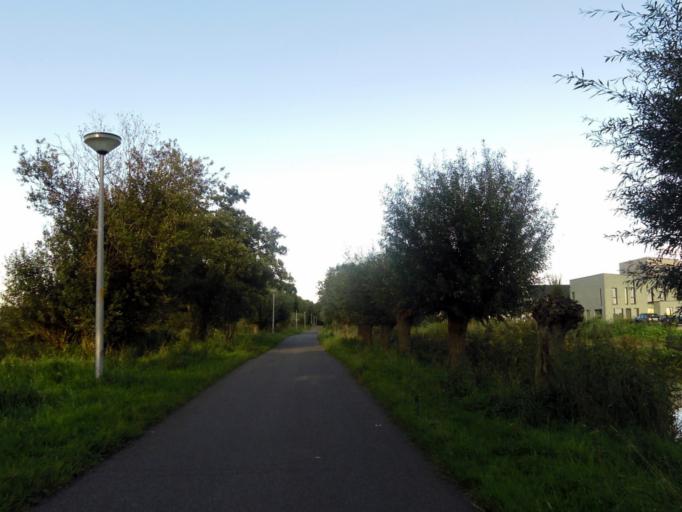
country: NL
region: South Holland
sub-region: Gemeente Alphen aan den Rijn
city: Alphen aan den Rijn
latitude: 52.1221
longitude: 4.6358
